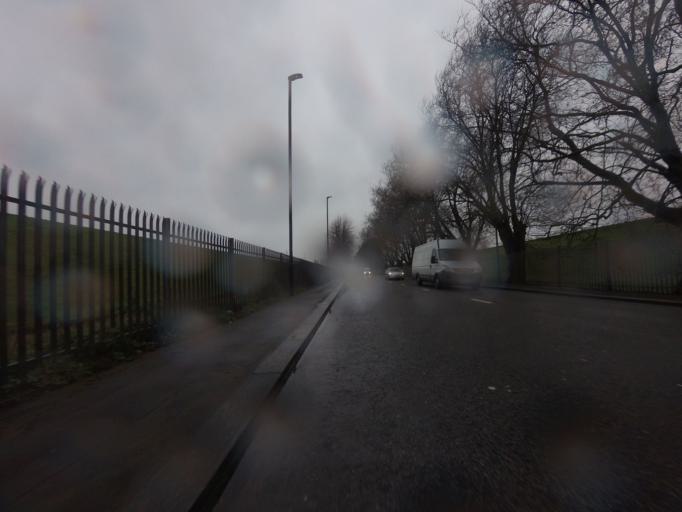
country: GB
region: England
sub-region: Greater London
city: Walthamstow
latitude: 51.6386
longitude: -0.0210
